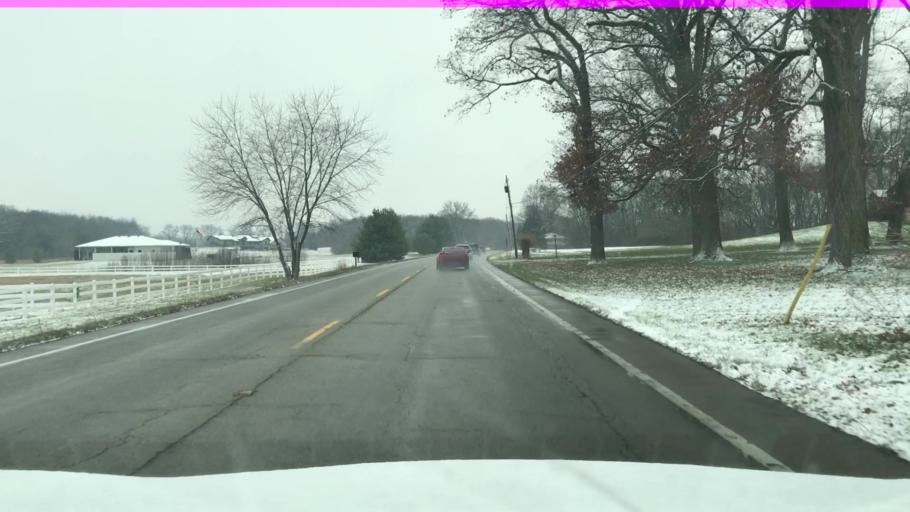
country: US
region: Indiana
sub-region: Delaware County
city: Yorktown
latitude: 40.1584
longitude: -85.5316
